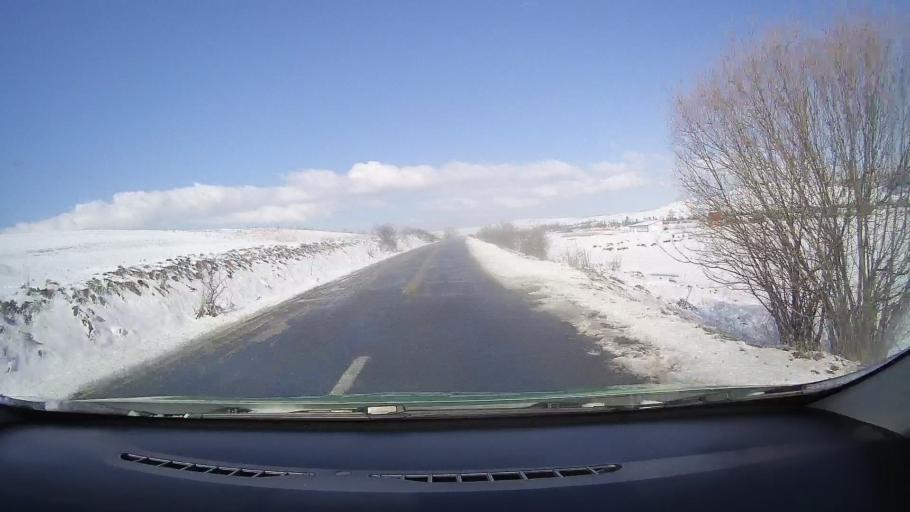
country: RO
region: Sibiu
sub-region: Comuna Rosia
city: Rosia
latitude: 45.8297
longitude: 24.3125
